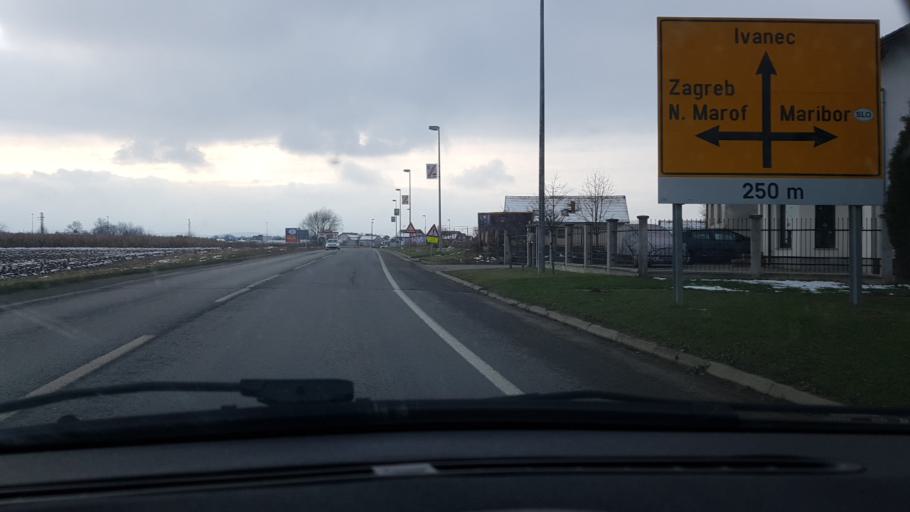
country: HR
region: Varazdinska
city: Jalkovec
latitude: 46.2944
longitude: 16.3092
